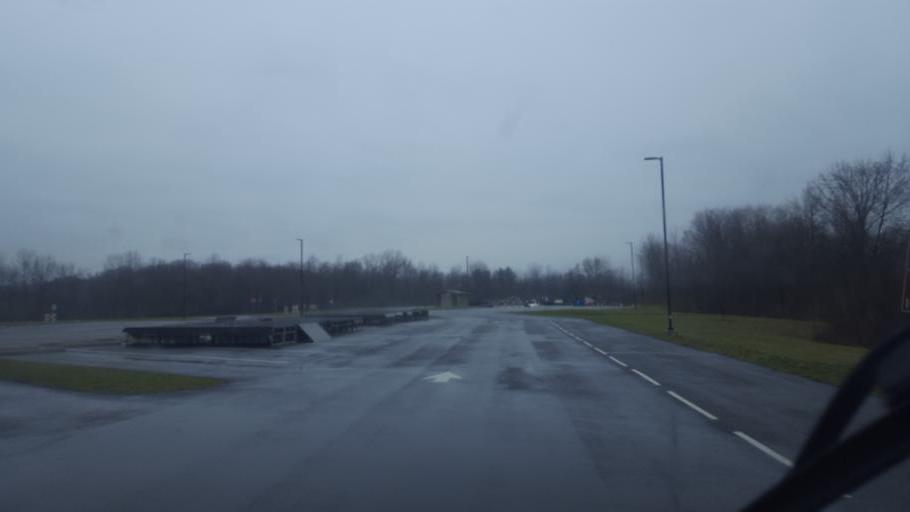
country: US
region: Ohio
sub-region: Delaware County
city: Lewis Center
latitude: 40.2124
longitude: -82.9723
